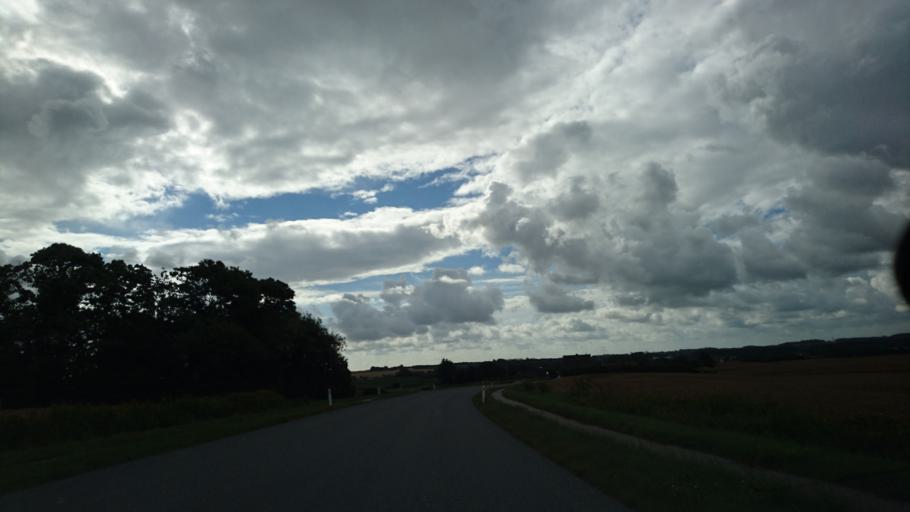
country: DK
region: North Denmark
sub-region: Hjorring Kommune
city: Tars
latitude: 57.3522
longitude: 10.2233
